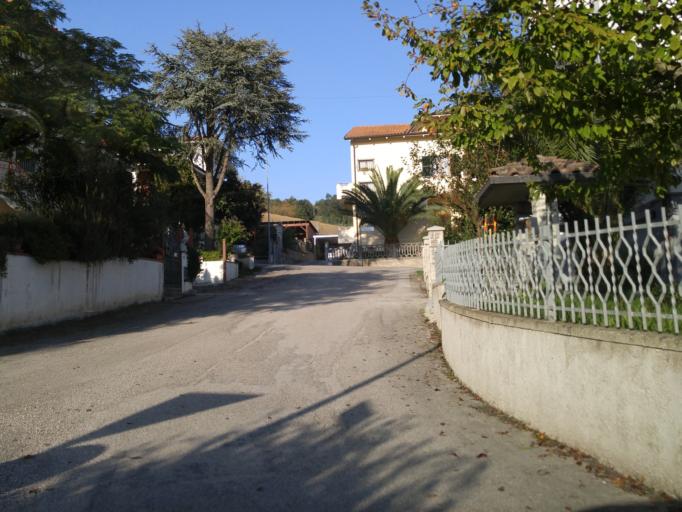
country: IT
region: The Marches
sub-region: Provincia di Pesaro e Urbino
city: Montefelcino
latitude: 43.7234
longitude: 12.8392
